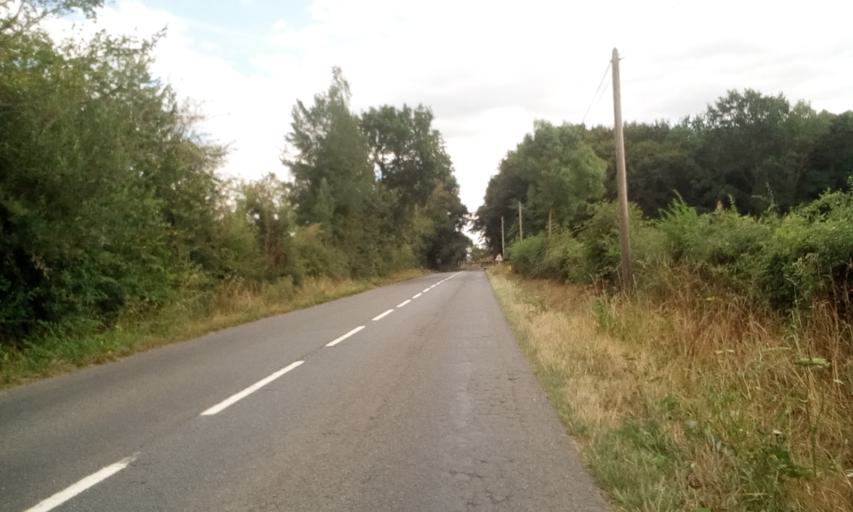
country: FR
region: Lower Normandy
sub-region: Departement du Calvados
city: Troarn
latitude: 49.1620
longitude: -0.1767
